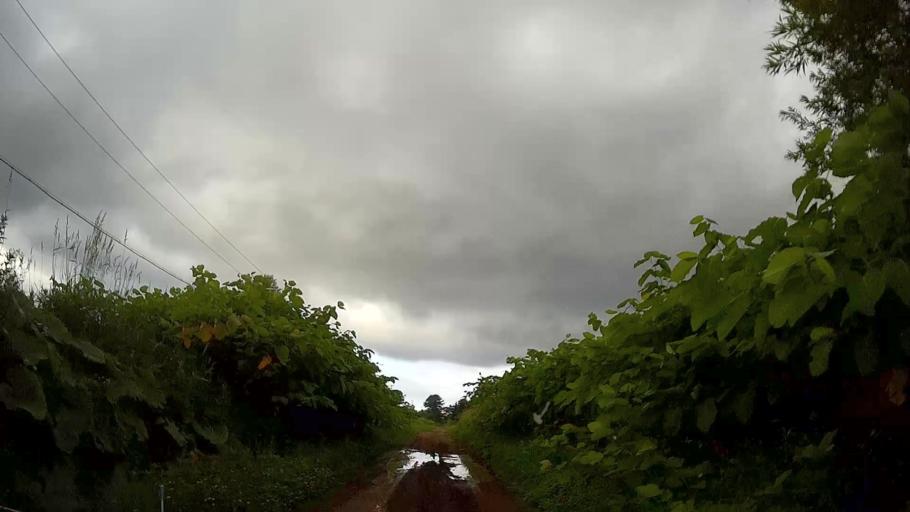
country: JP
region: Hokkaido
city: Nanae
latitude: 42.1214
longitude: 140.4064
